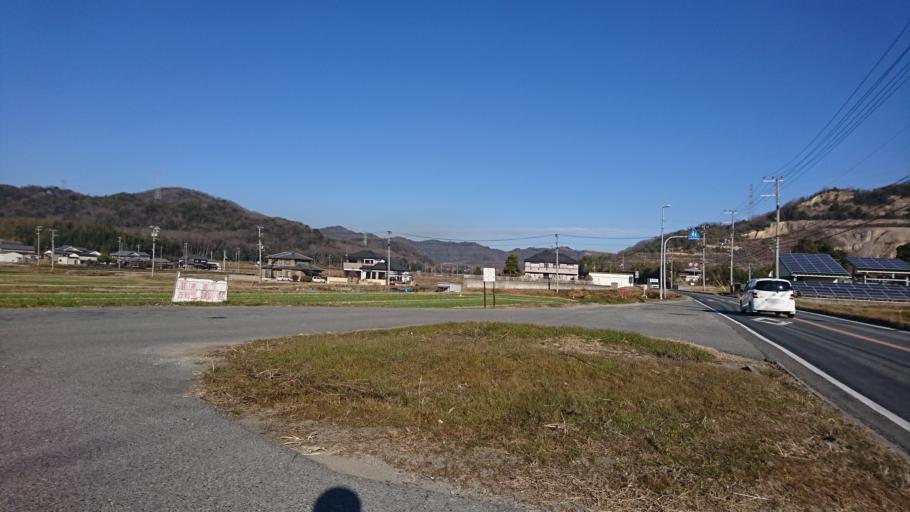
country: JP
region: Hyogo
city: Kakogawacho-honmachi
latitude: 34.8384
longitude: 134.8390
